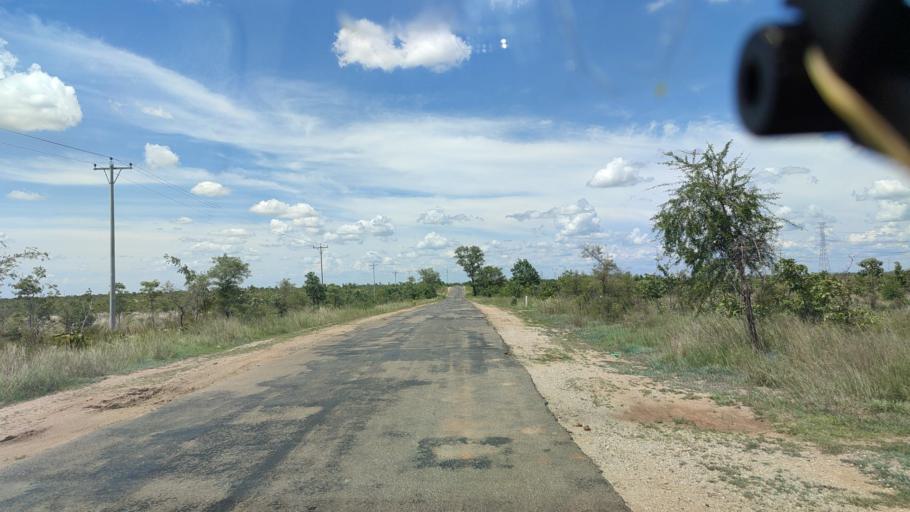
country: MM
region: Magway
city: Taungdwingyi
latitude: 19.7436
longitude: 95.4125
